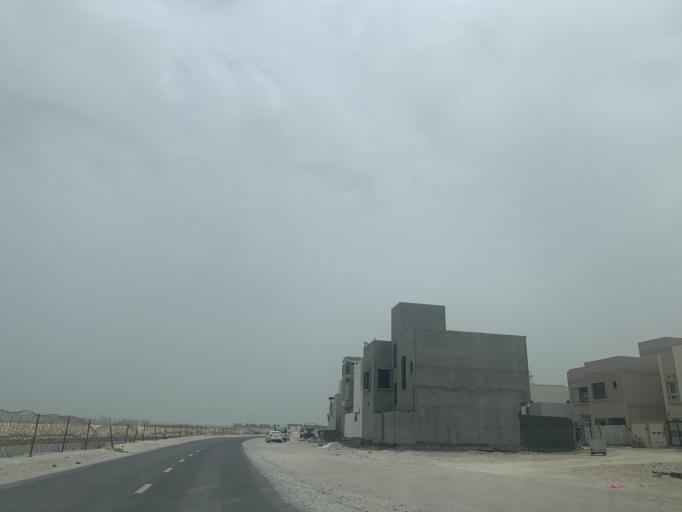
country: BH
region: Northern
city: Sitrah
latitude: 26.1727
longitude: 50.6271
